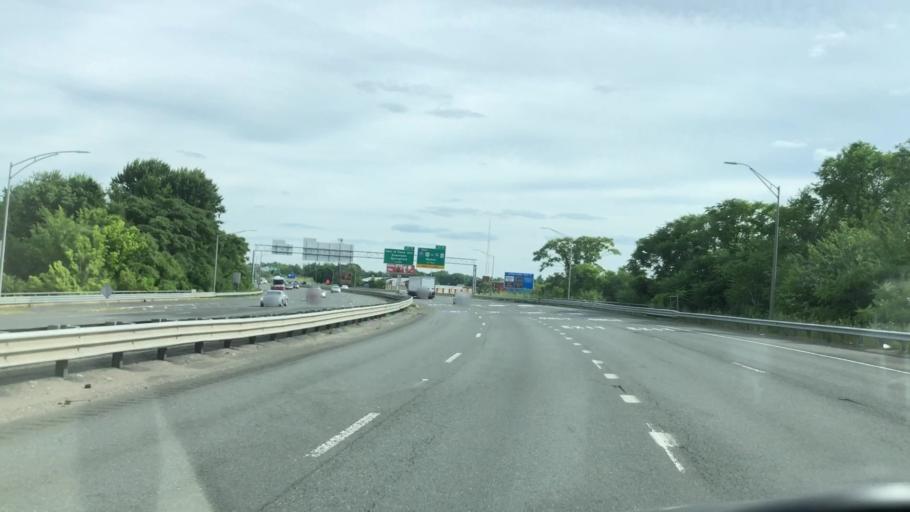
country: US
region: Massachusetts
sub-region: Hampden County
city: West Springfield
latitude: 42.1207
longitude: -72.6097
